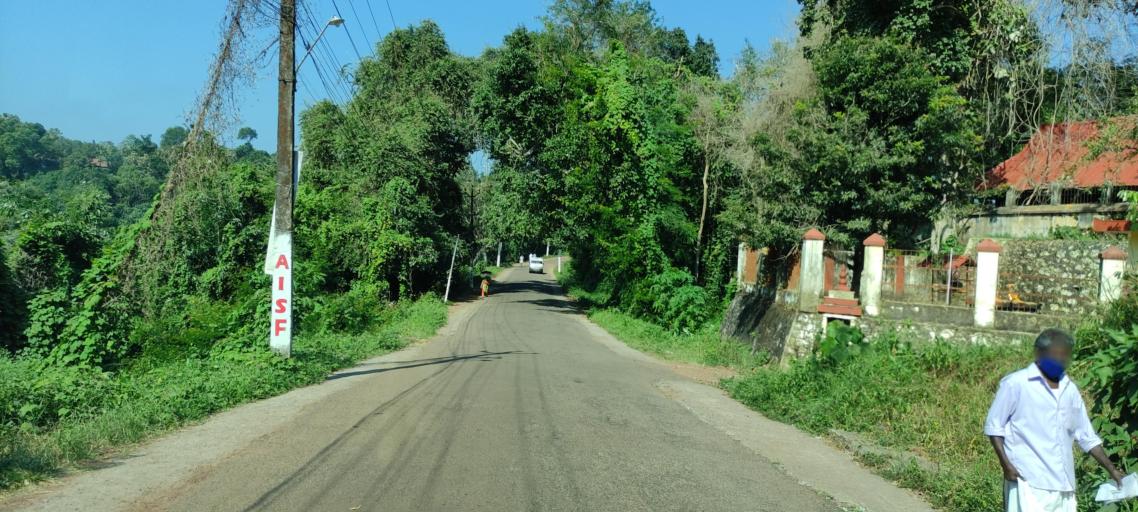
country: IN
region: Kerala
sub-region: Kollam
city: Panmana
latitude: 9.0411
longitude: 76.6296
